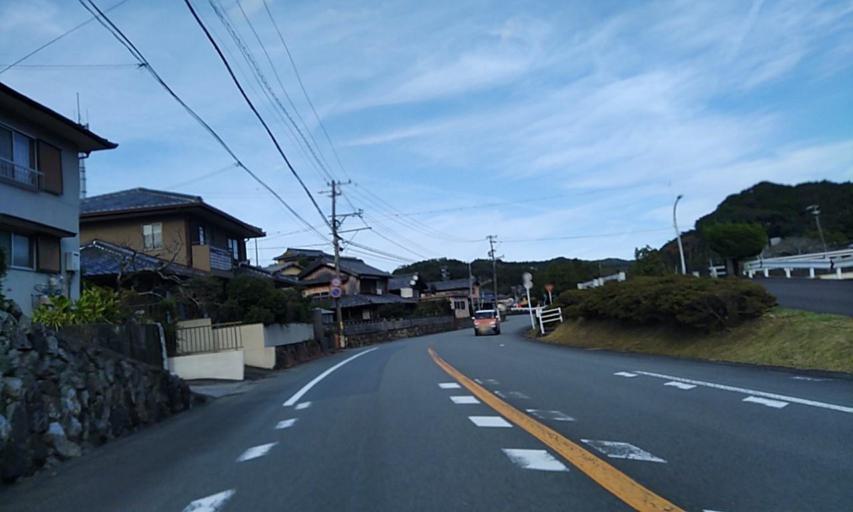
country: JP
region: Mie
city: Ise
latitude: 34.3432
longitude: 136.7298
